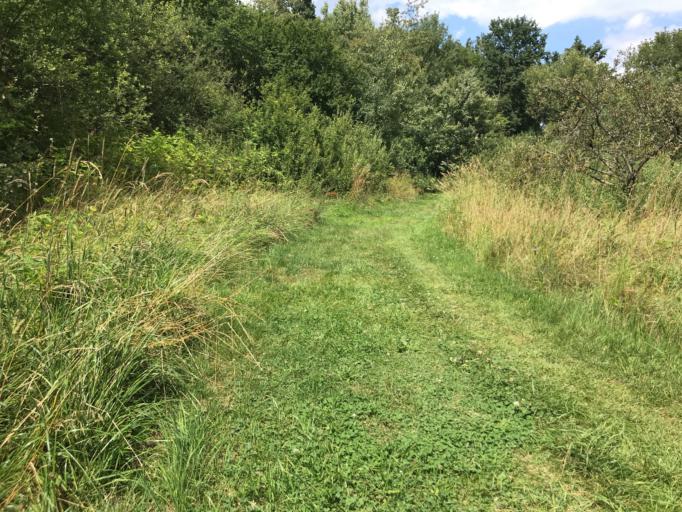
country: CZ
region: Jihocesky
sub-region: Okres Jindrichuv Hradec
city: Lomnice nad Luznici
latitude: 49.0879
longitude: 14.7127
